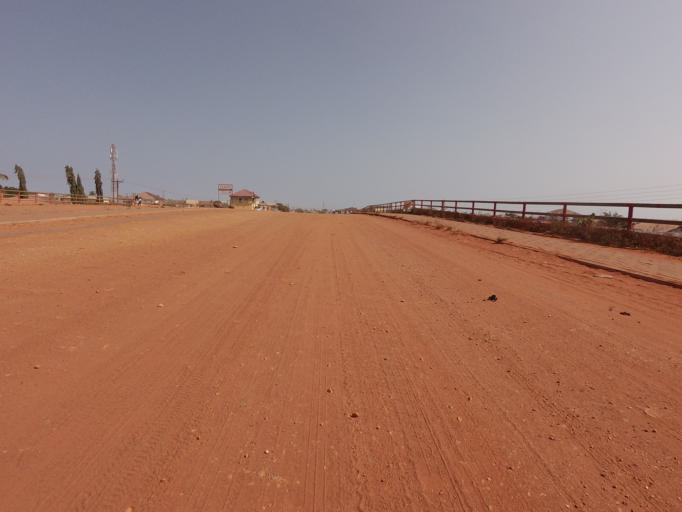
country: GH
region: Greater Accra
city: Teshi Old Town
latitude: 5.6200
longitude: -0.1249
